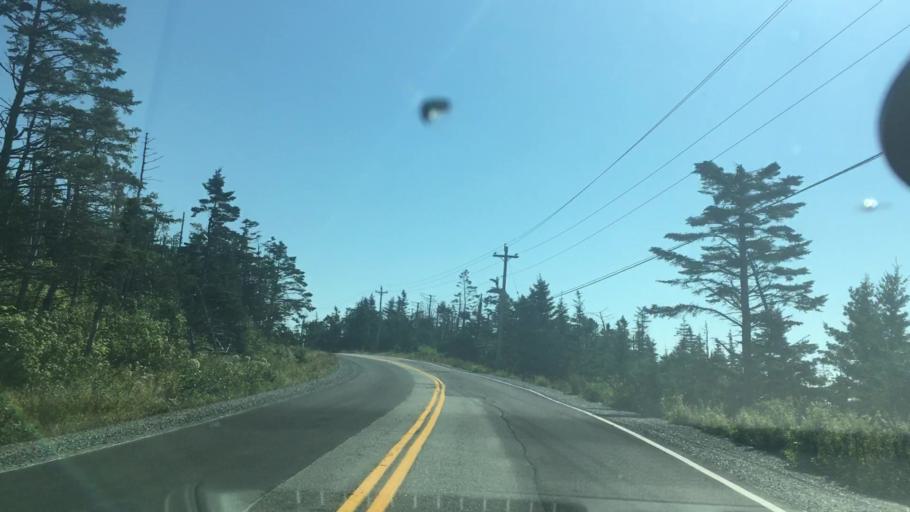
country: CA
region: Nova Scotia
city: New Glasgow
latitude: 44.9162
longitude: -62.3190
